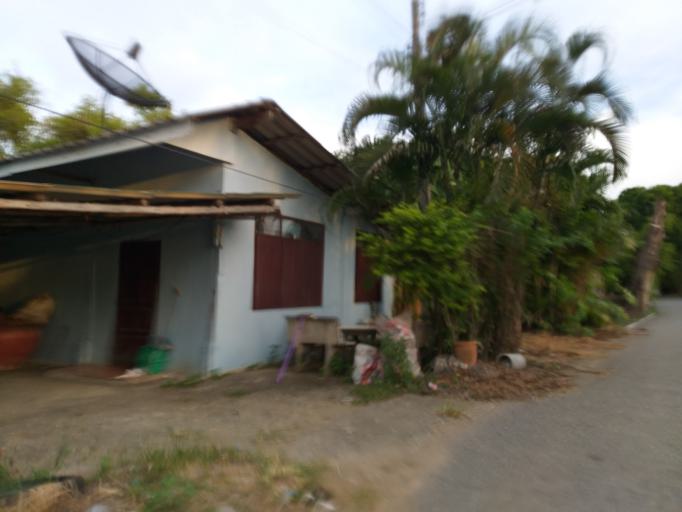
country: TH
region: Pathum Thani
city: Ban Lam Luk Ka
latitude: 14.0036
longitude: 100.7984
